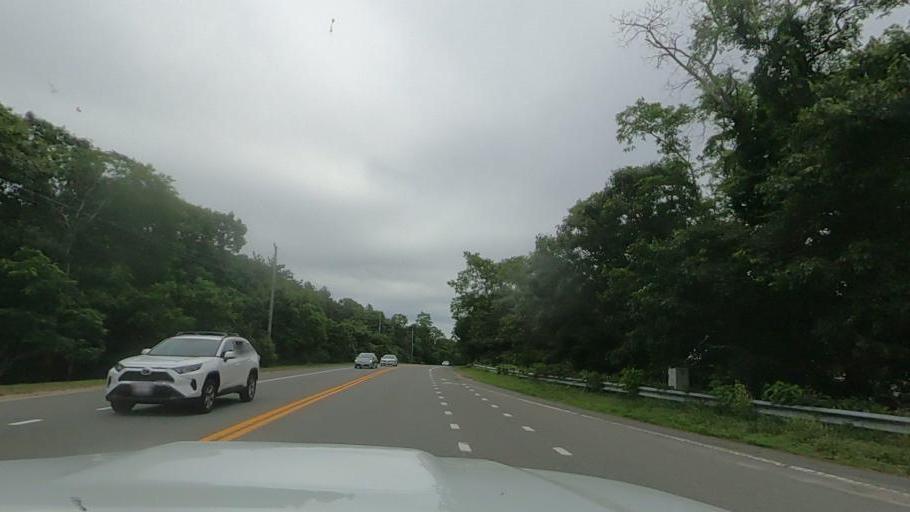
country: US
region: Massachusetts
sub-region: Barnstable County
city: Truro
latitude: 41.9998
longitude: -70.0497
